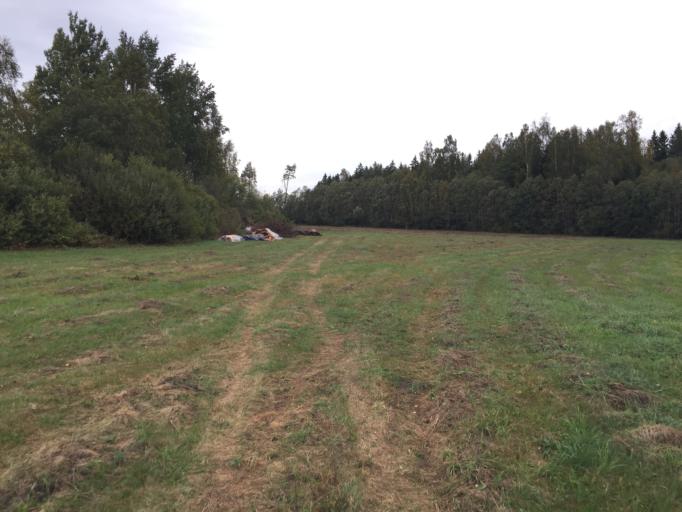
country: LV
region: Malpils
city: Malpils
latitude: 56.9323
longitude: 24.9453
